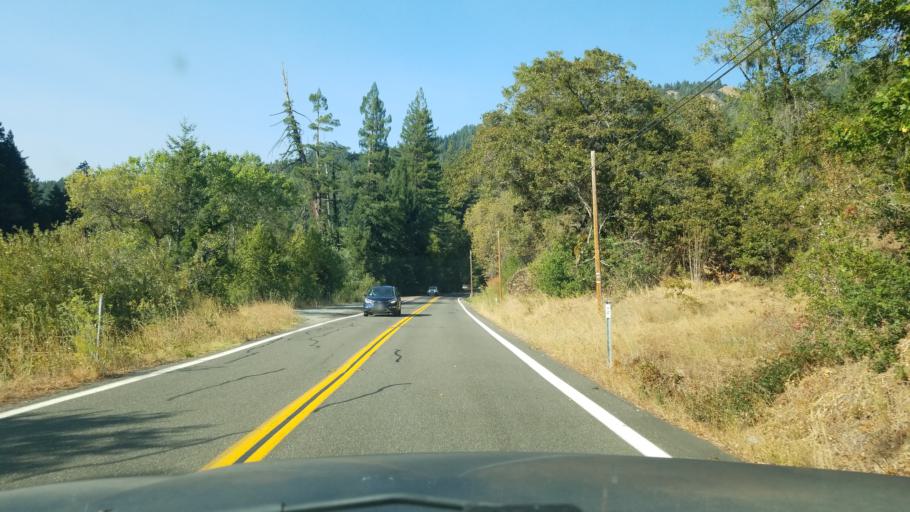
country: US
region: California
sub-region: Humboldt County
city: Redway
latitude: 40.1899
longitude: -123.7692
